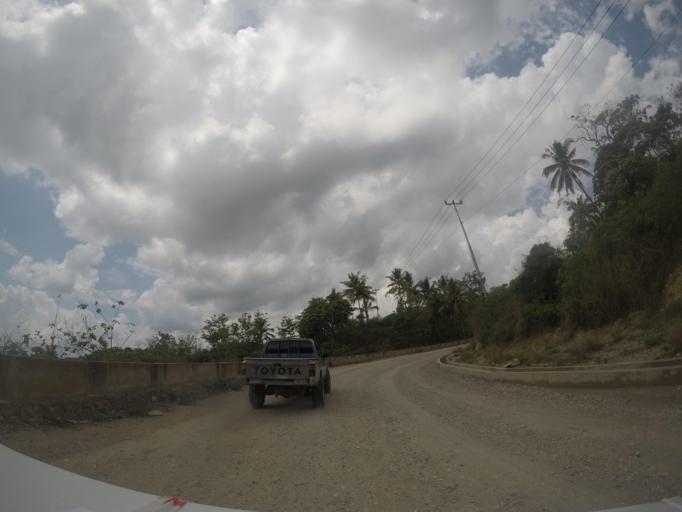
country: TL
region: Baucau
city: Baucau
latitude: -8.5329
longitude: 126.4259
